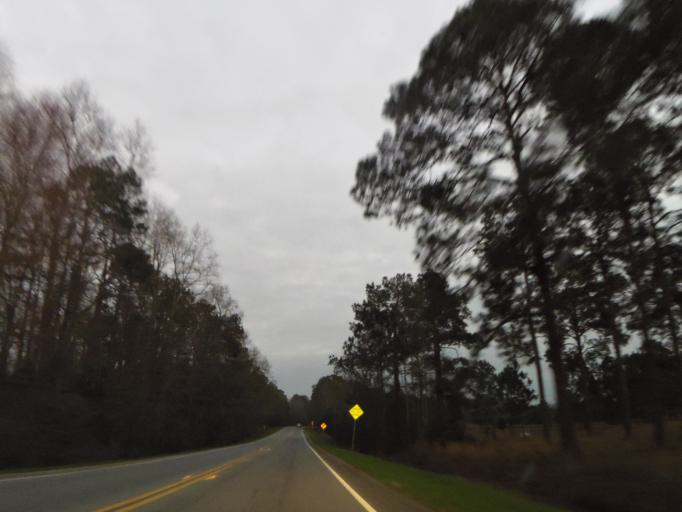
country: US
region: Georgia
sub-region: Worth County
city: Sylvester
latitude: 31.4164
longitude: -83.9436
